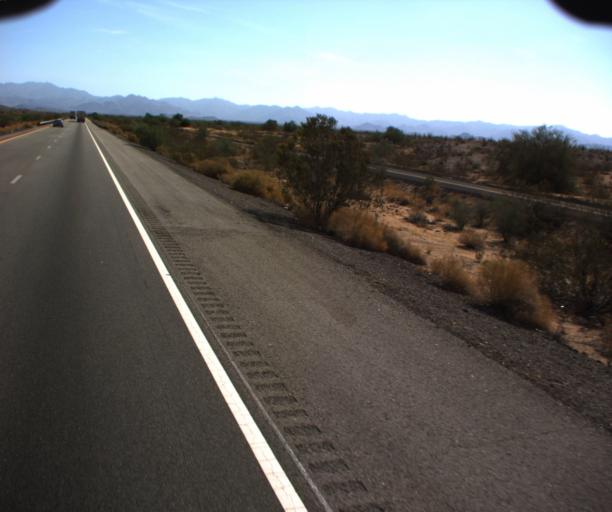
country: US
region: Arizona
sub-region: Mohave County
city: Desert Hills
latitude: 34.7778
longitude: -114.1839
